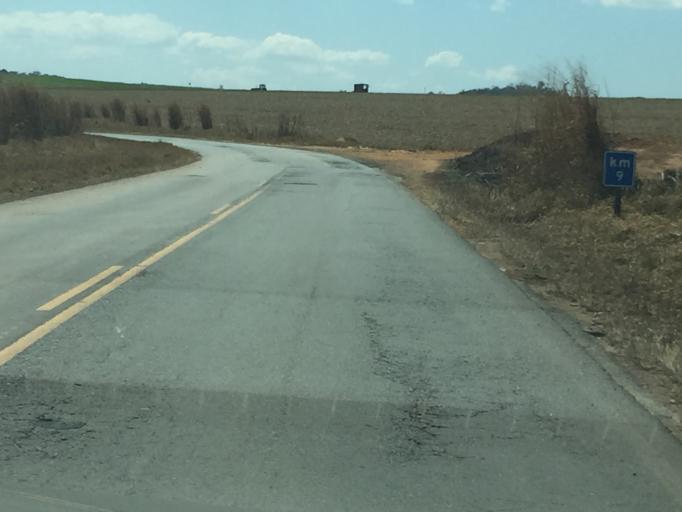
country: BR
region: Sao Paulo
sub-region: Moji-Guacu
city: Mogi-Gaucu
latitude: -22.3616
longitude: -46.8694
